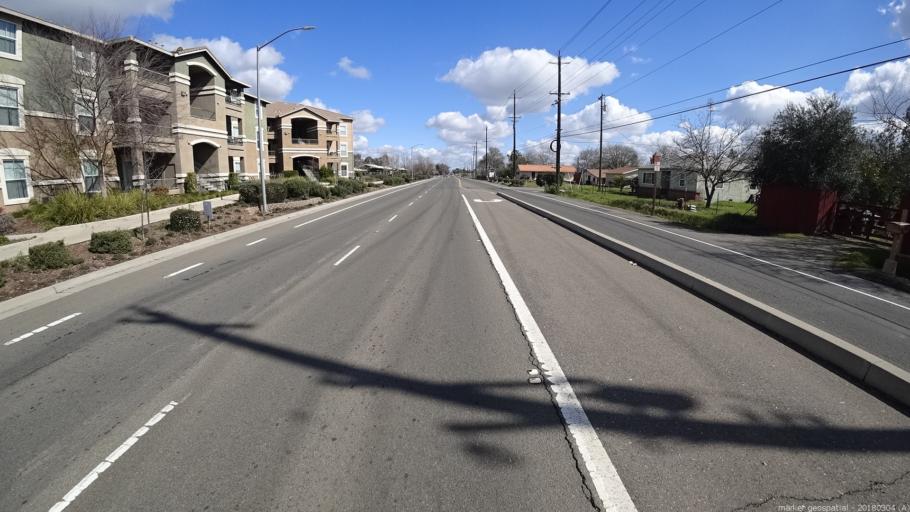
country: US
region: California
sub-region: Sacramento County
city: Vineyard
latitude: 38.4817
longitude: -121.3413
